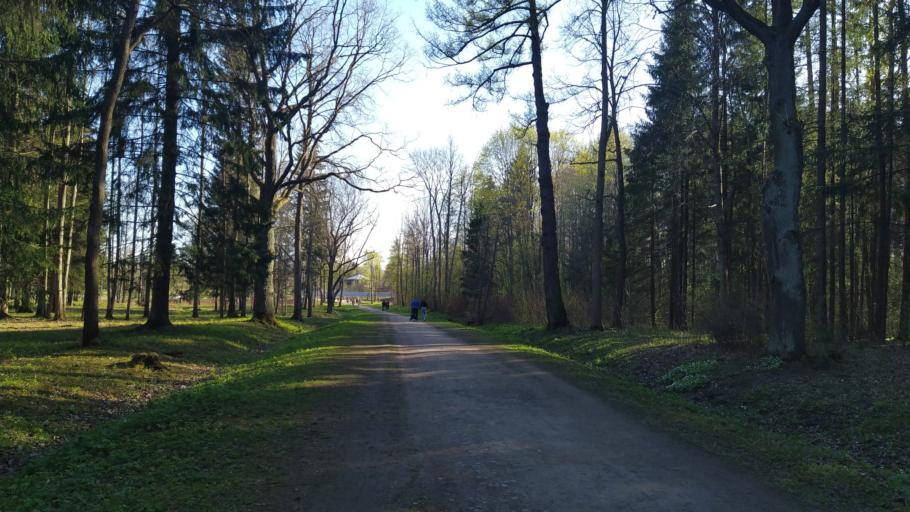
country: RU
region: St.-Petersburg
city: Aleksandrovskaya
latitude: 59.7115
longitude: 30.3470
